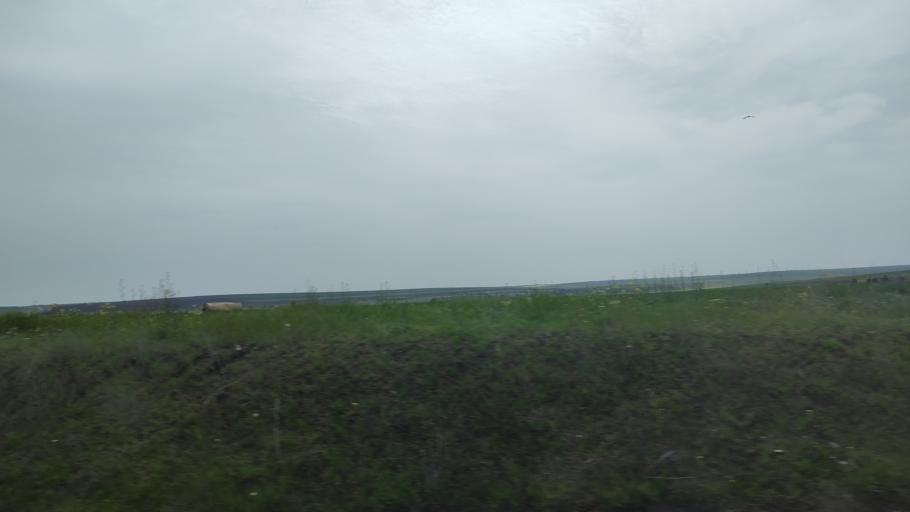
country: RO
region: Constanta
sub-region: Oras Murfatlar
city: Siminoc
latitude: 44.1424
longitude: 28.3574
